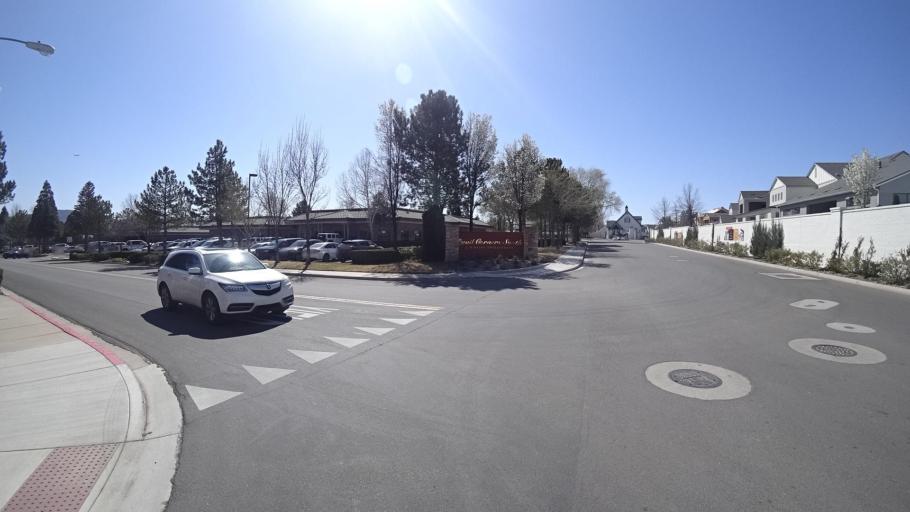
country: US
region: Nevada
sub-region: Washoe County
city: Reno
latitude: 39.4735
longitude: -119.8002
